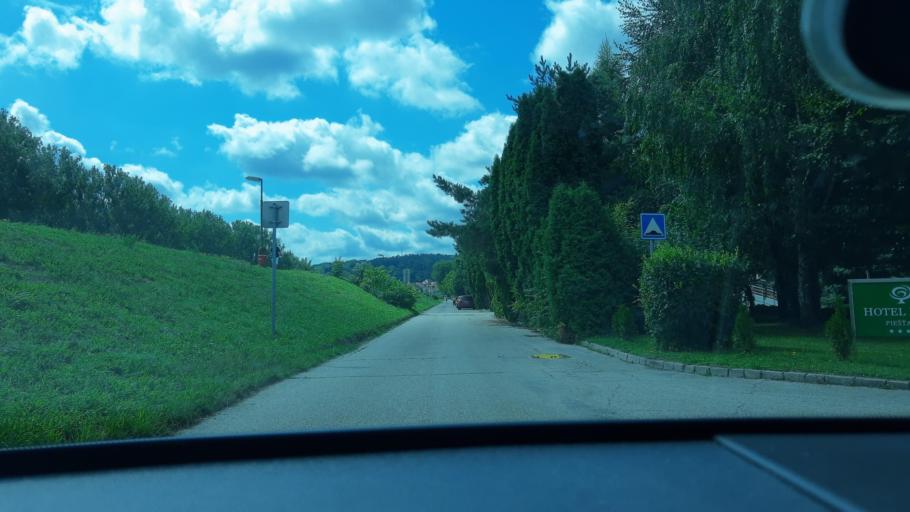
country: SK
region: Trnavsky
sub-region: Okres Trnava
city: Piestany
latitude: 48.5957
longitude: 17.8406
